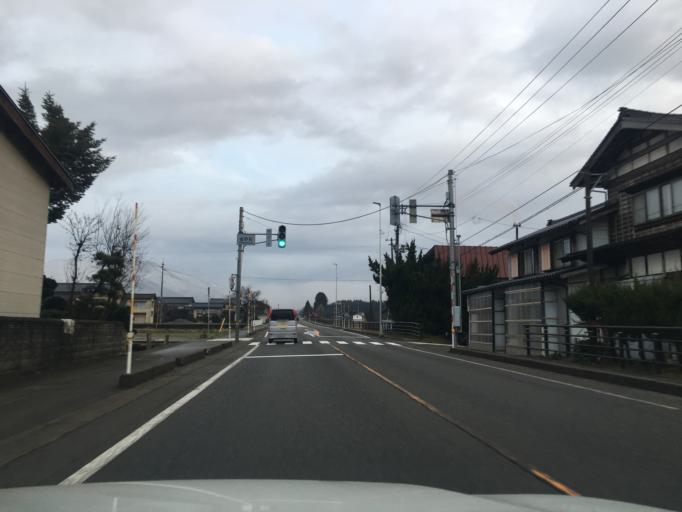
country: JP
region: Niigata
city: Murakami
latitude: 38.3258
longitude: 139.5556
